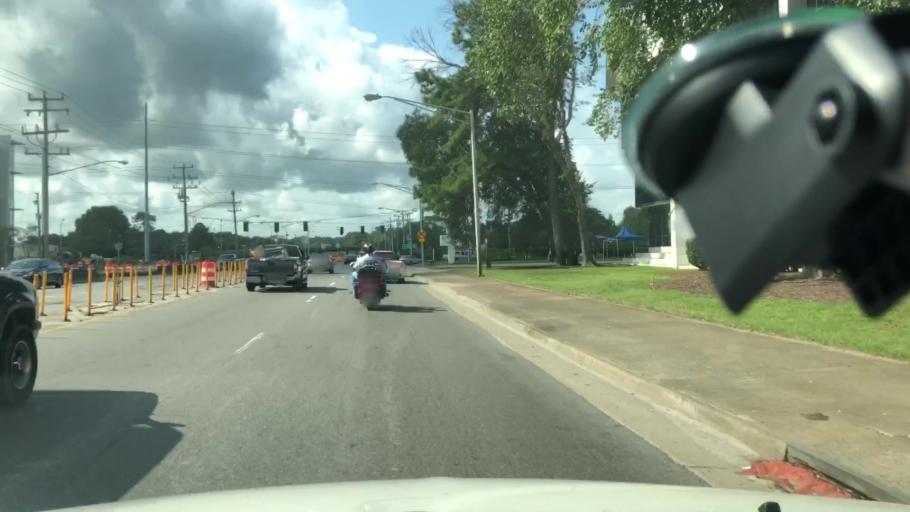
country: US
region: Virginia
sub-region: City of Chesapeake
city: Chesapeake
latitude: 36.8419
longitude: -76.1583
